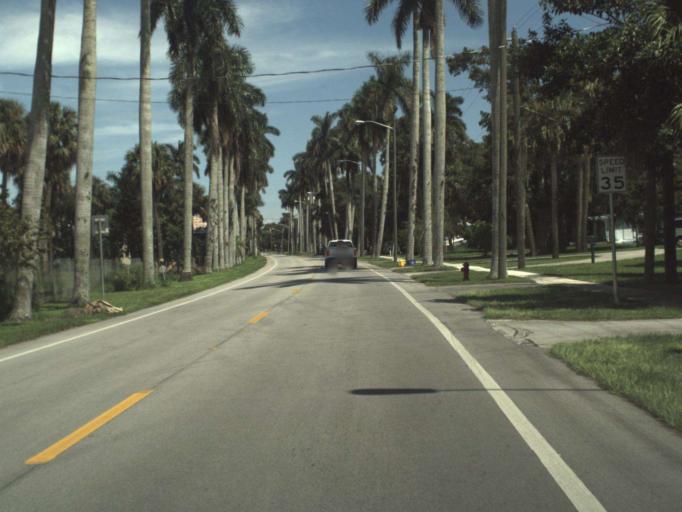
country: US
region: Florida
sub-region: Palm Beach County
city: Pahokee
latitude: 26.8349
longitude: -80.6495
